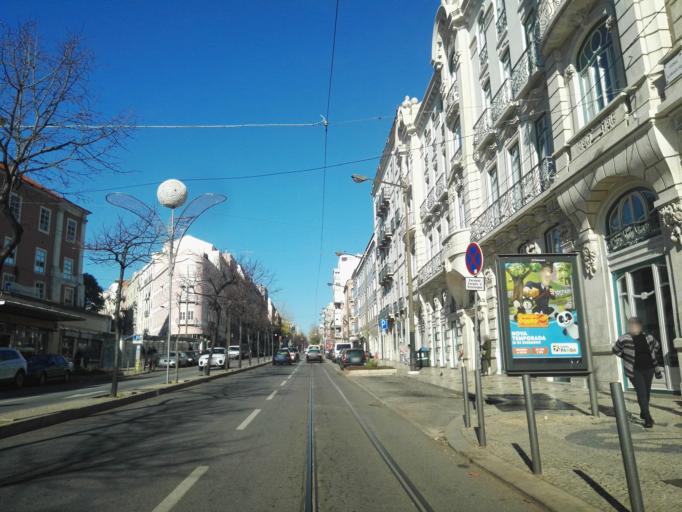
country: PT
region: Lisbon
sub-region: Lisbon
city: Lisbon
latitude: 38.7203
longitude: -9.1355
